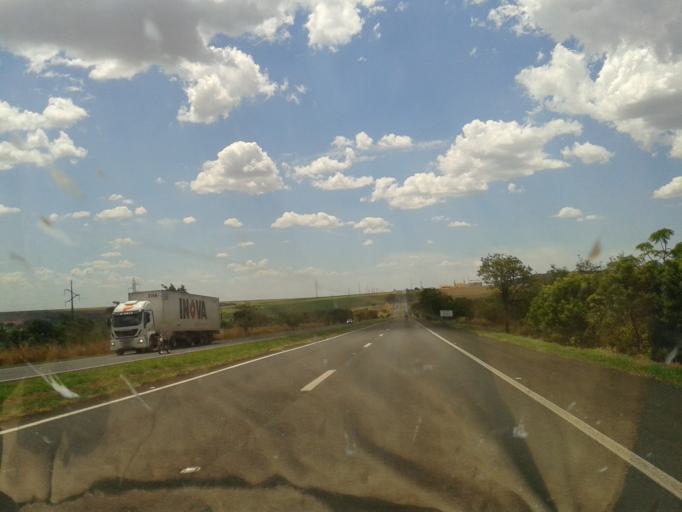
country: BR
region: Minas Gerais
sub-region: Uberlandia
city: Uberlandia
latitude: -19.0975
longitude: -48.1822
